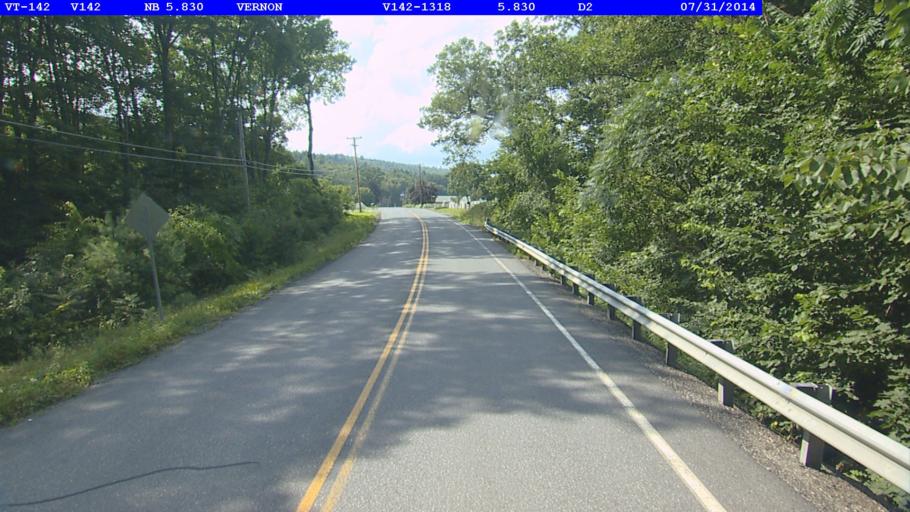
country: US
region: New Hampshire
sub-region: Cheshire County
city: Hinsdale
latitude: 42.7868
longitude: -72.5295
